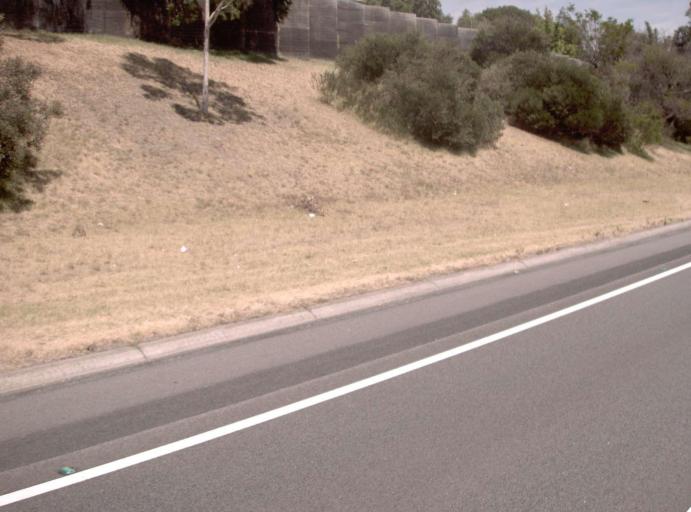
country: AU
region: Victoria
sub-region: Monash
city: Chadstone
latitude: -37.8859
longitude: 145.1024
